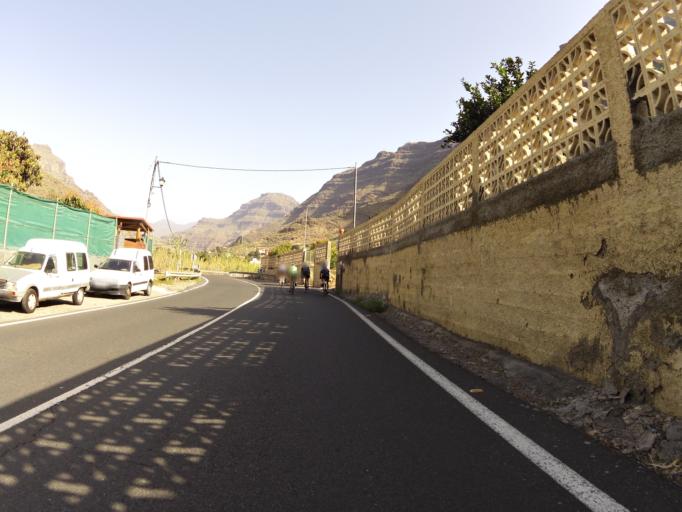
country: ES
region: Canary Islands
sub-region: Provincia de Las Palmas
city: Puerto Rico
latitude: 27.8339
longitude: -15.6593
